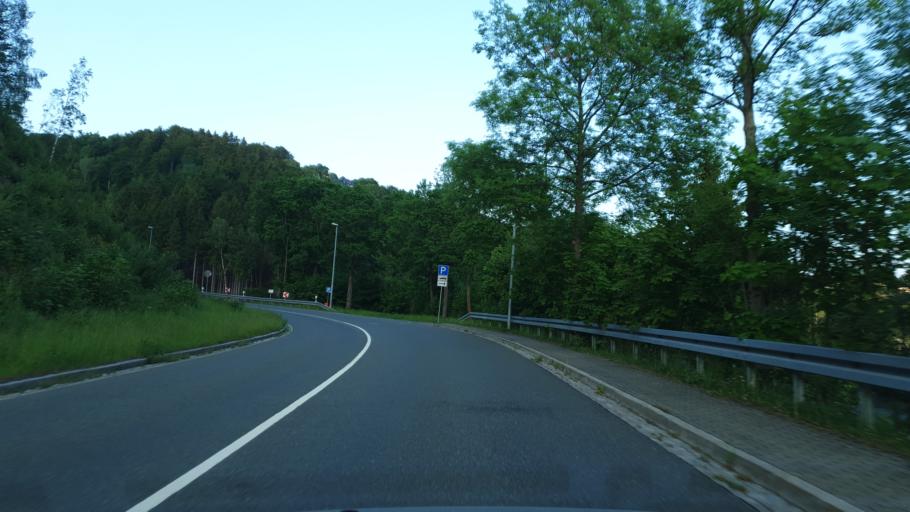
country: DE
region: Saxony
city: Klingenthal
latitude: 50.3850
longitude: 12.4888
